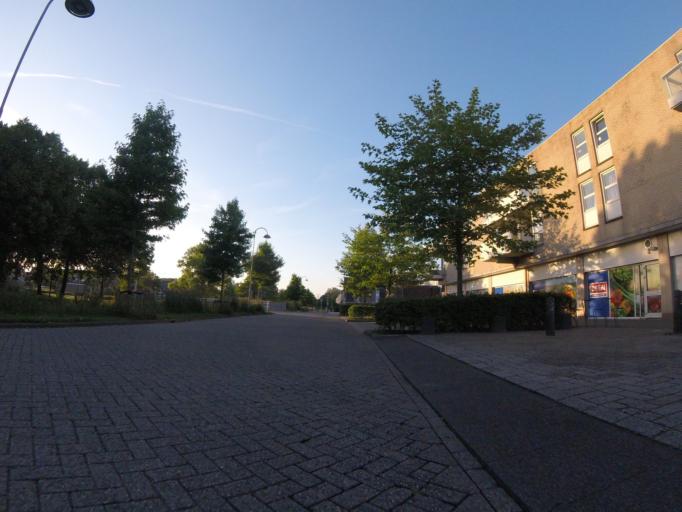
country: NL
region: North Holland
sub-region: Gemeente Haarlemmermeer
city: Hoofddorp
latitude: 52.3147
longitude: 4.6580
